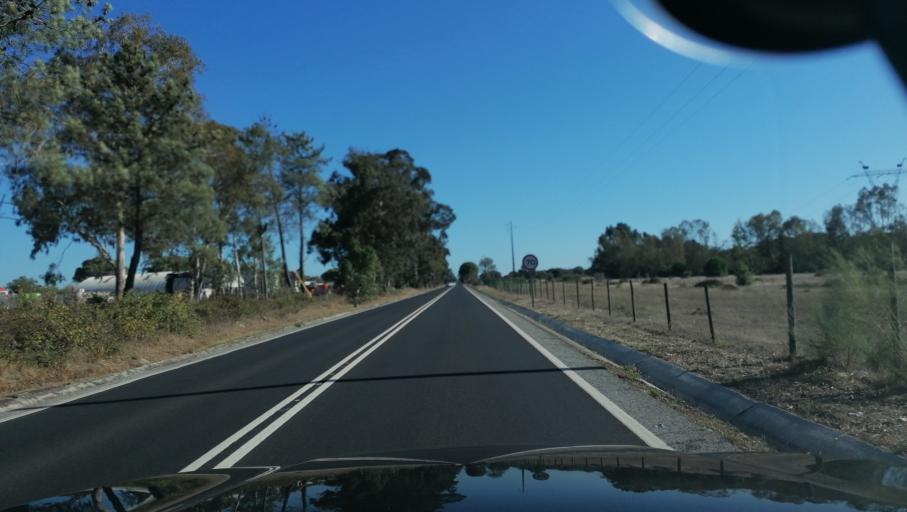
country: PT
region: Santarem
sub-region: Benavente
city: Poceirao
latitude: 38.8331
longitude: -8.8810
